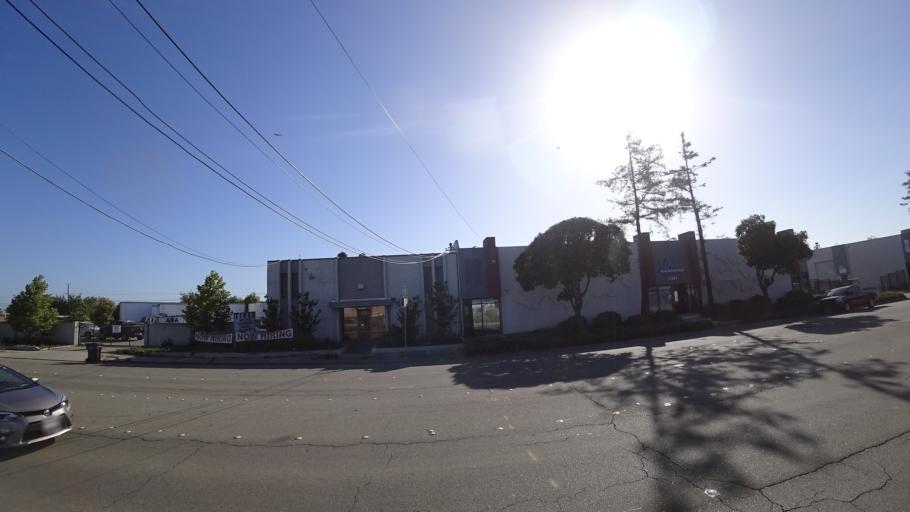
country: US
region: California
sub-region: Alameda County
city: Hayward
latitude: 37.6236
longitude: -122.1031
